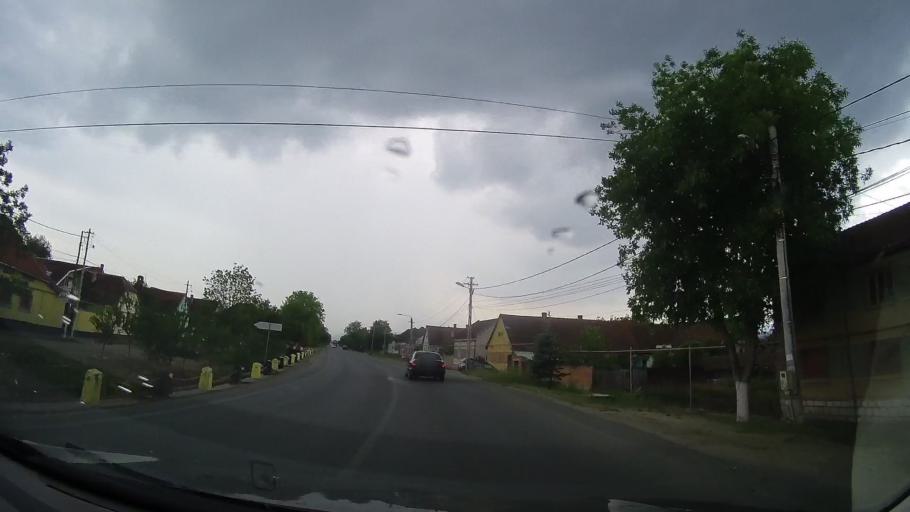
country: RO
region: Caras-Severin
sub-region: Municipiul Caransebes
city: Caransebes
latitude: 45.4023
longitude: 22.2239
